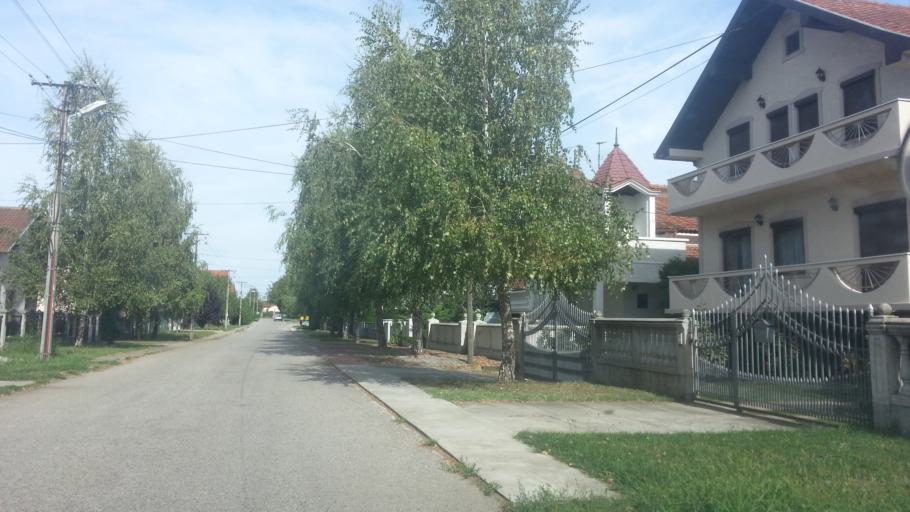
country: RS
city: Novi Banovci
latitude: 44.9473
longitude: 20.2790
